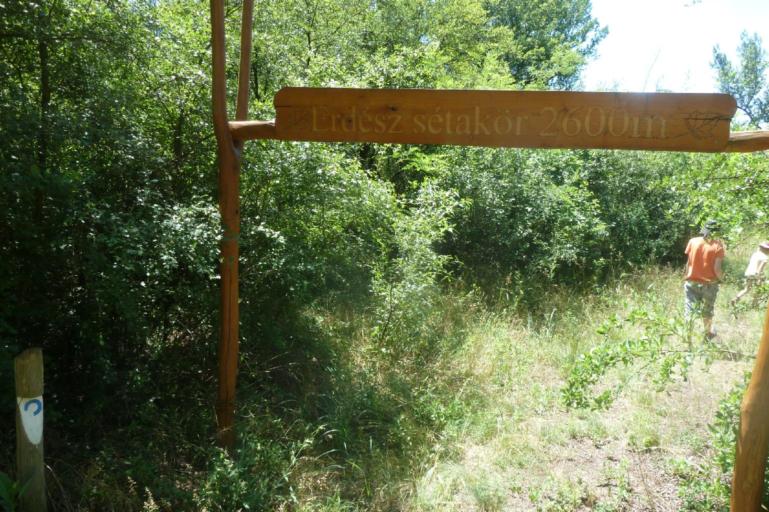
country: HU
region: Pest
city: Kakucs
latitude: 47.2841
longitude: 19.4101
